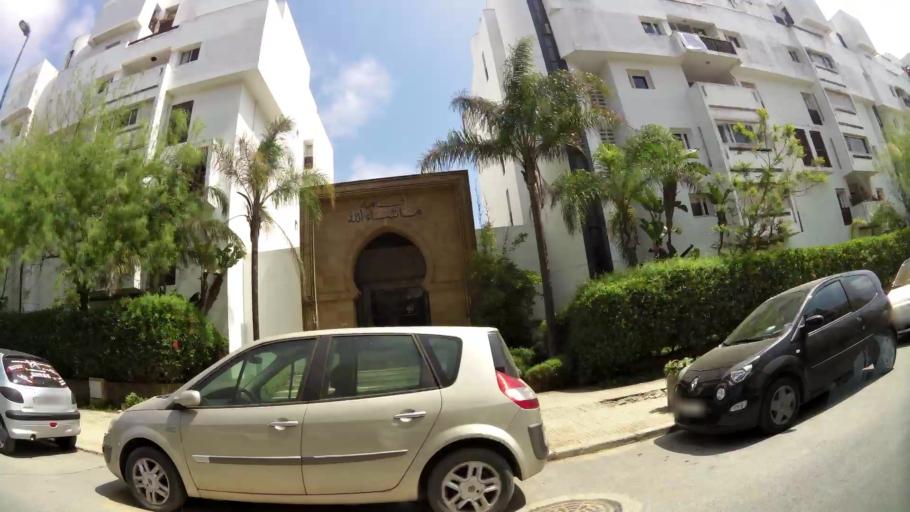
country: MA
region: Rabat-Sale-Zemmour-Zaer
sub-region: Rabat
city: Rabat
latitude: 33.9881
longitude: -6.8477
